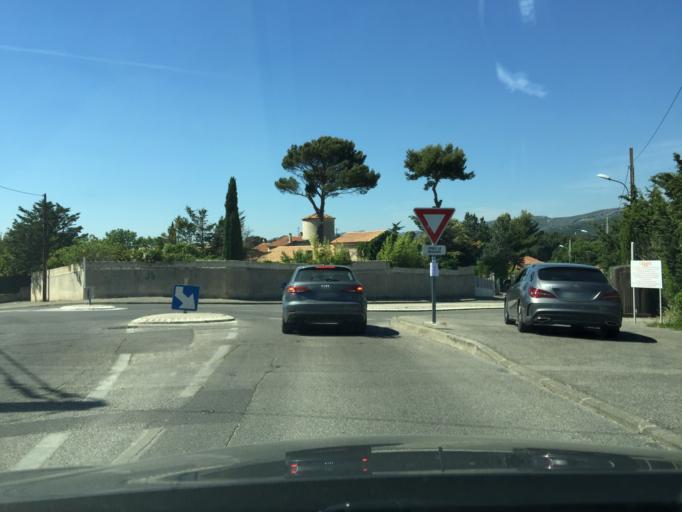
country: FR
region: Provence-Alpes-Cote d'Azur
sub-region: Departement des Bouches-du-Rhone
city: La Penne-sur-Huveaune
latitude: 43.2752
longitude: 5.5291
